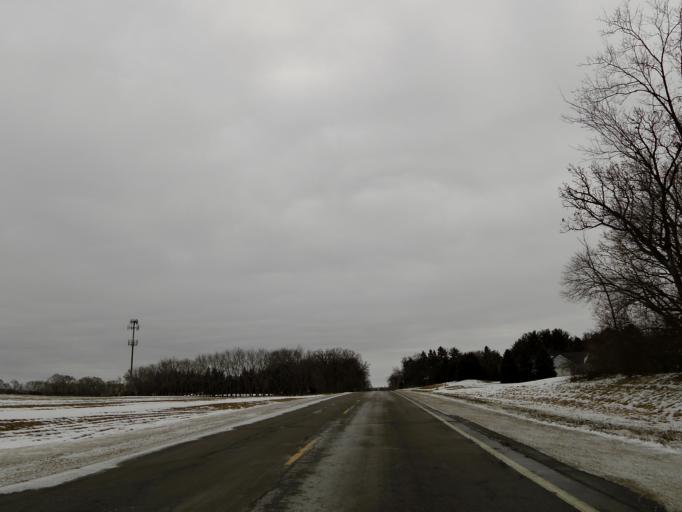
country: US
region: Minnesota
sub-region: Washington County
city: Cottage Grove
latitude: 44.8005
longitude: -92.8933
